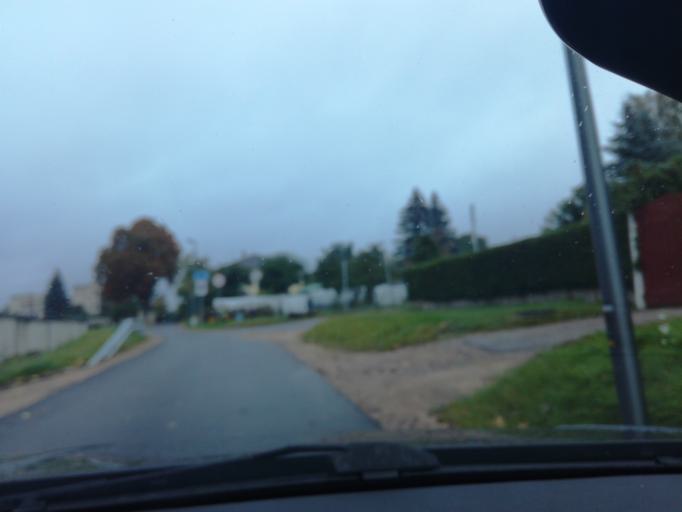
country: LT
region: Alytaus apskritis
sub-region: Alytus
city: Alytus
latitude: 54.3991
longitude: 24.0708
